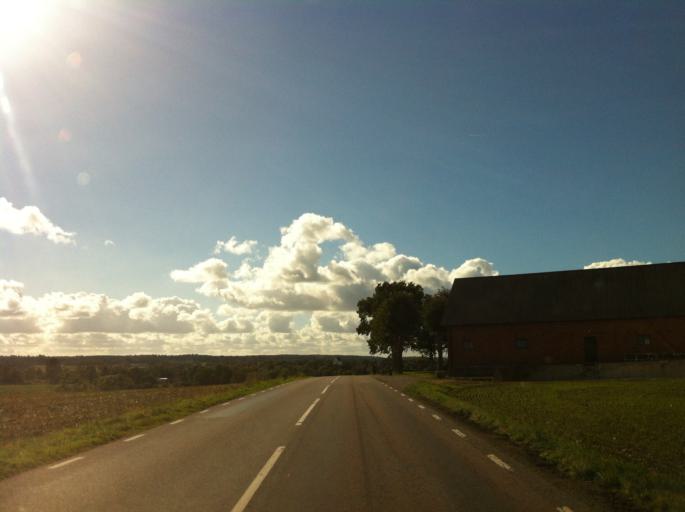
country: SE
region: Skane
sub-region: Sjobo Kommun
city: Sjoebo
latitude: 55.6444
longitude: 13.7940
